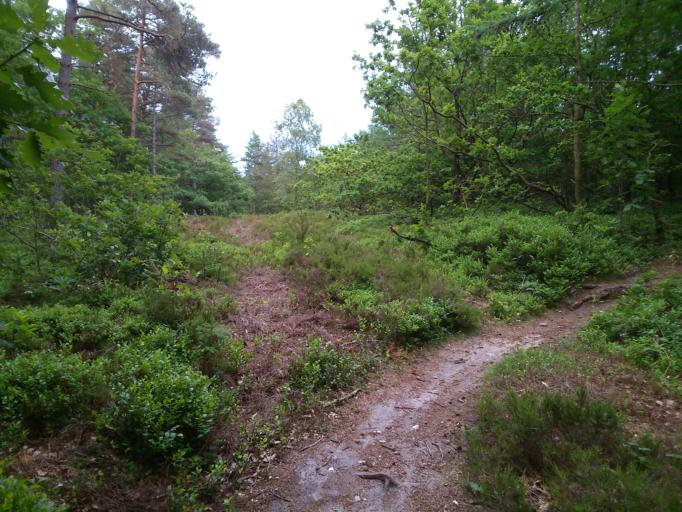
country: DK
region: Central Jutland
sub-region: Ringkobing-Skjern Kommune
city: Skjern
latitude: 55.9946
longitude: 8.4383
